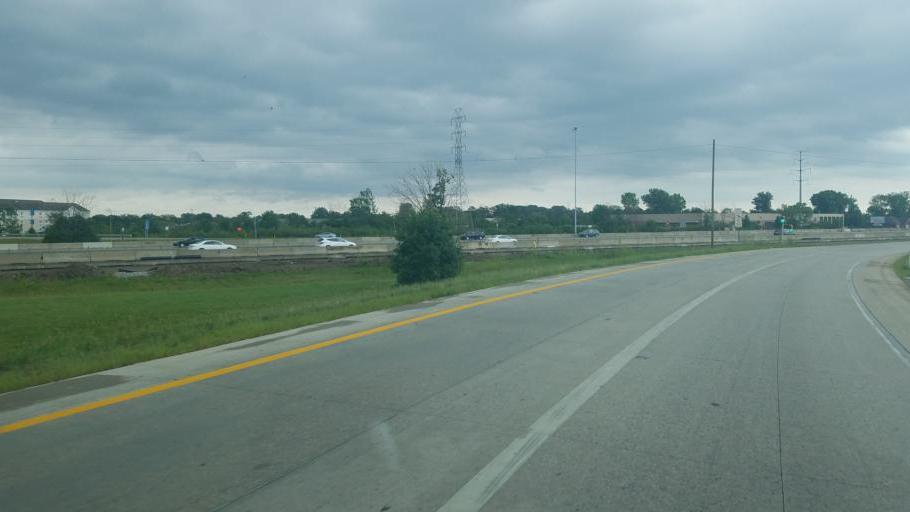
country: US
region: Ohio
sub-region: Franklin County
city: Lincoln Village
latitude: 40.0013
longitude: -83.1193
